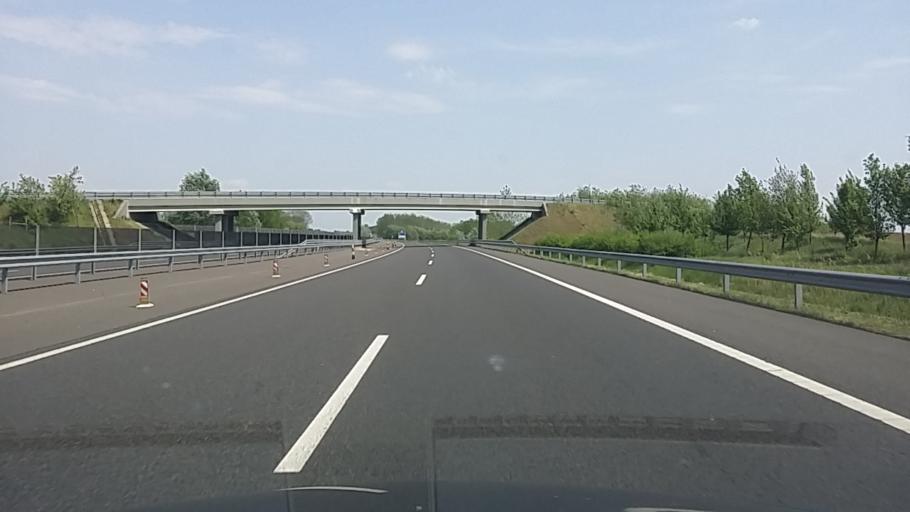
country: HU
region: Szabolcs-Szatmar-Bereg
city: Kalmanhaza
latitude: 47.8960
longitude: 21.6268
